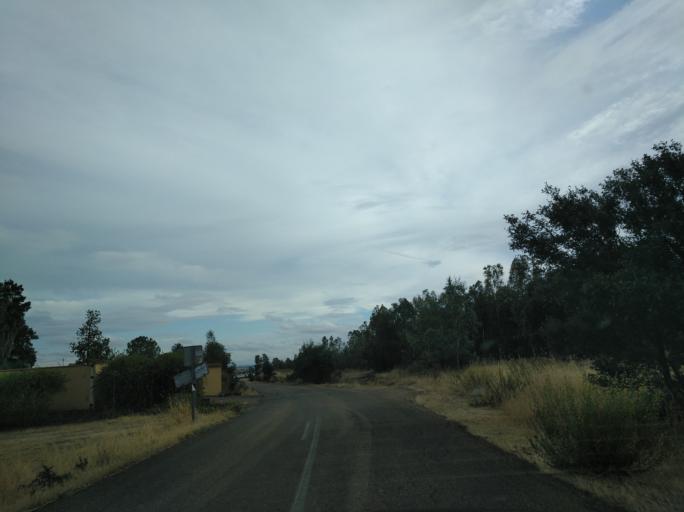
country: ES
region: Extremadura
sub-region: Provincia de Badajoz
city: Badajoz
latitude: 38.8920
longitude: -7.0170
